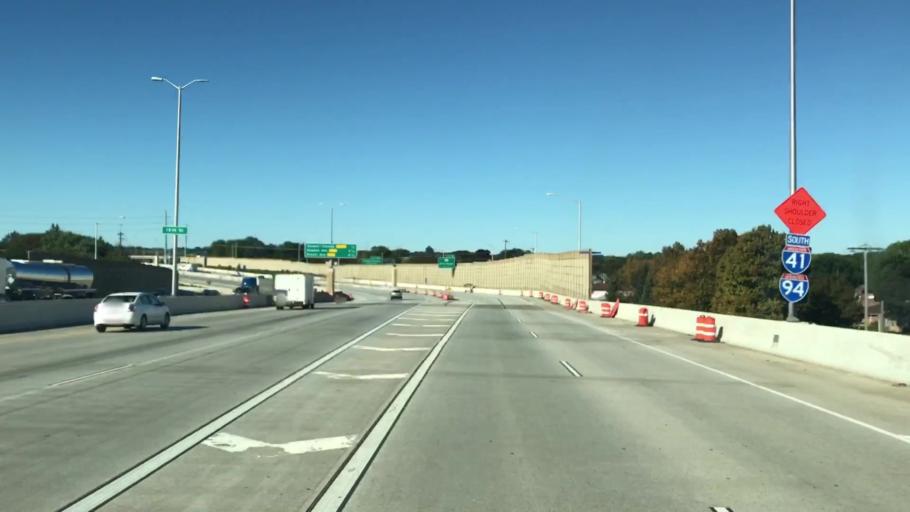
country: US
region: Wisconsin
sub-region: Milwaukee County
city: Saint Francis
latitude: 42.9661
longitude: -87.9285
